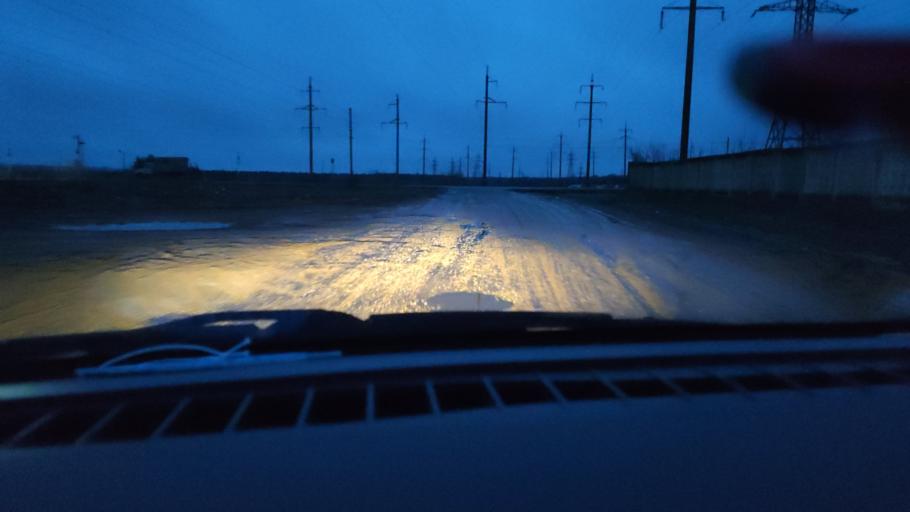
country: RU
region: Udmurtiya
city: Mozhga
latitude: 56.4351
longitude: 52.2506
